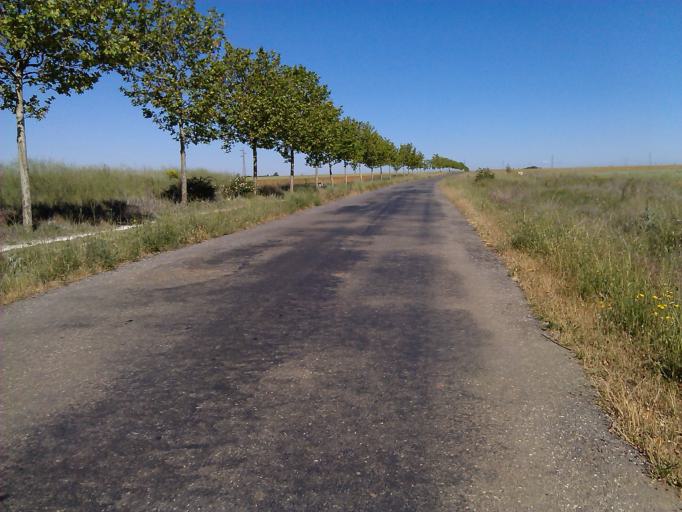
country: ES
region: Castille and Leon
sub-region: Provincia de Leon
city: Bercianos del Real Camino
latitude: 42.4045
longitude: -5.1832
